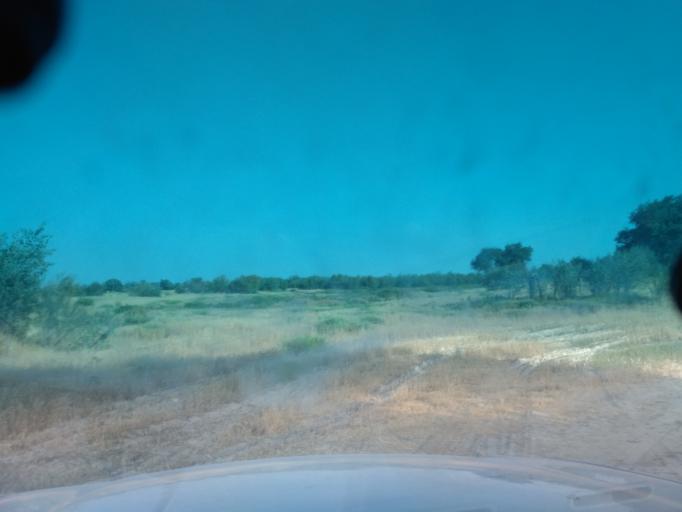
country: TJ
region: Viloyati Sughd
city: Buston
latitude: 40.5603
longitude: 69.0773
